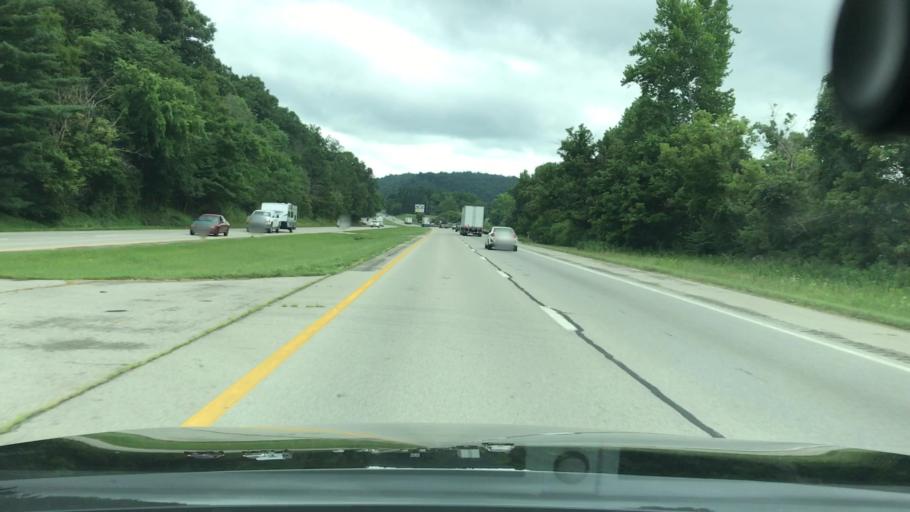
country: US
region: Ohio
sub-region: Jackson County
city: Jackson
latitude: 39.1768
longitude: -82.7486
